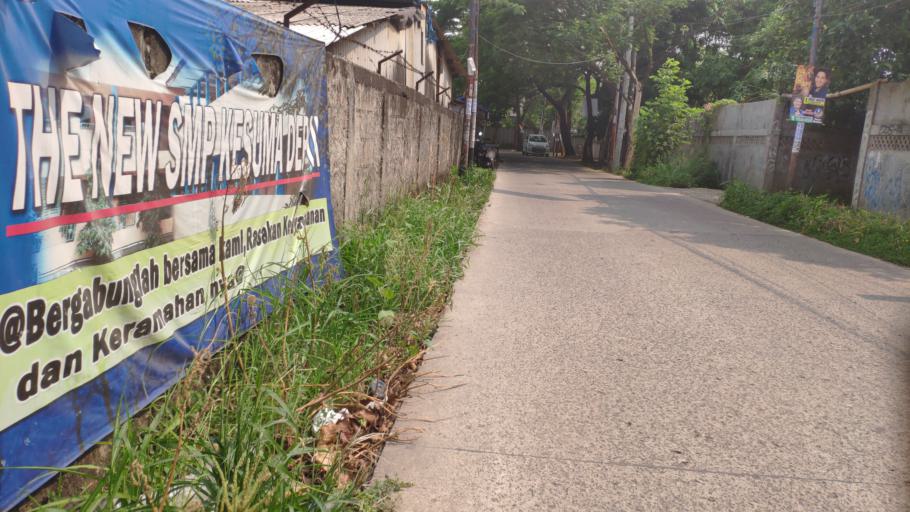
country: ID
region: West Java
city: Depok
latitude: -6.3801
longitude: 106.8017
